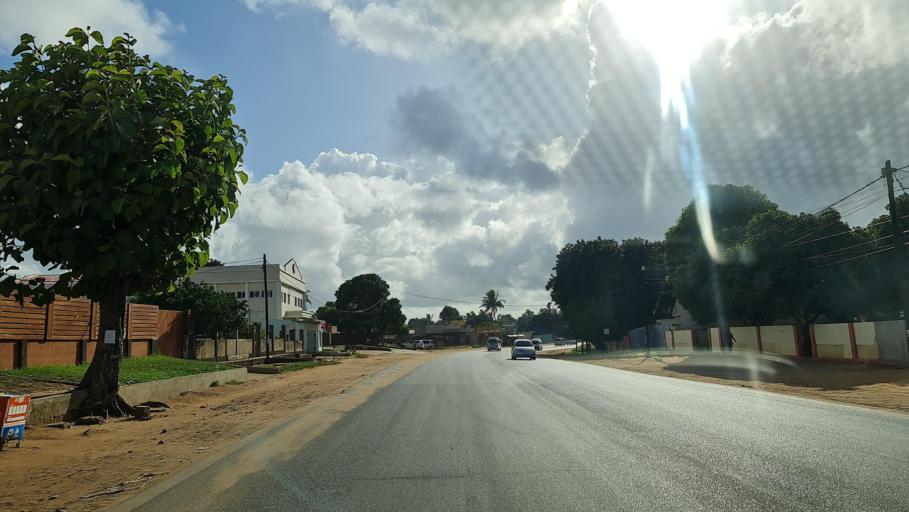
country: MZ
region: Gaza
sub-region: Xai-Xai District
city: Xai-Xai
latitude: -25.0558
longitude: 33.6667
